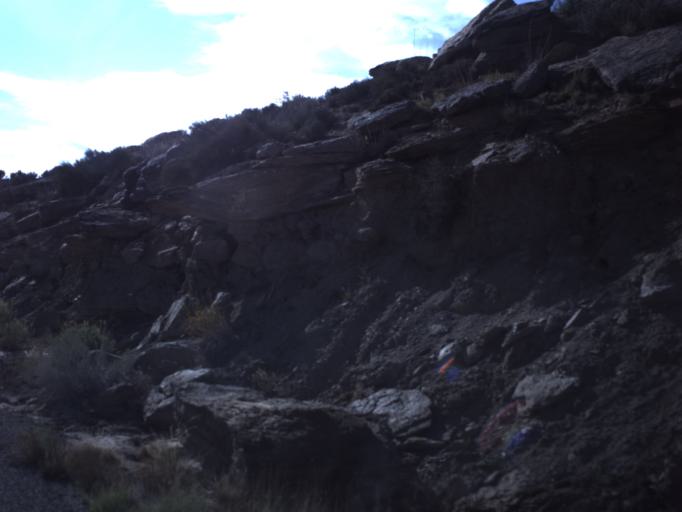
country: US
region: Utah
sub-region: San Juan County
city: Blanding
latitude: 37.3257
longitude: -109.3296
